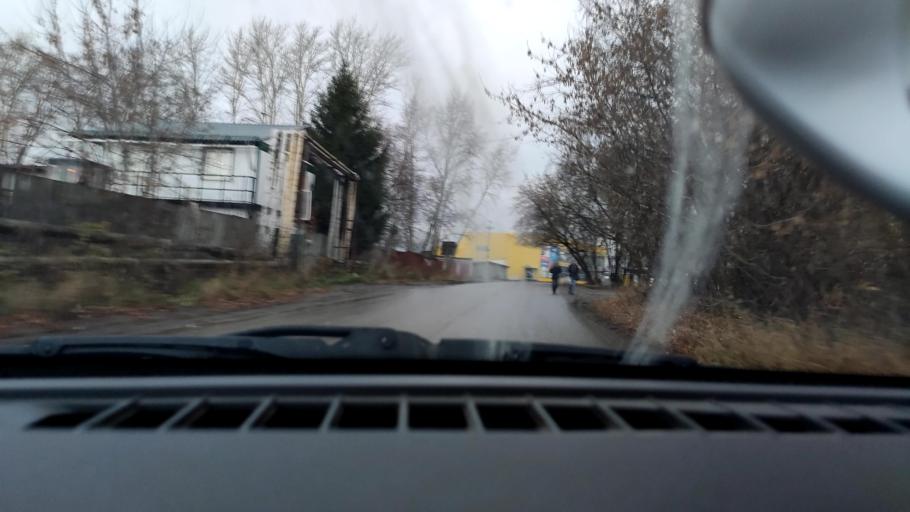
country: RU
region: Perm
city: Kondratovo
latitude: 57.9600
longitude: 56.1548
